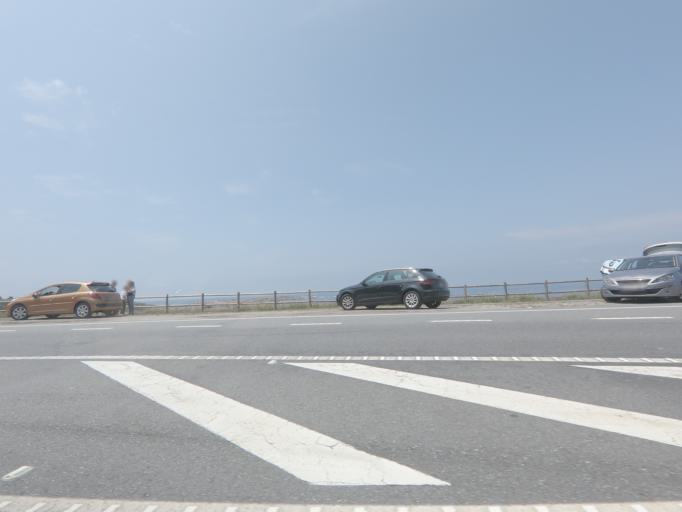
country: ES
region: Galicia
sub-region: Provincia de Pontevedra
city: Baiona
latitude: 42.1121
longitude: -8.8908
